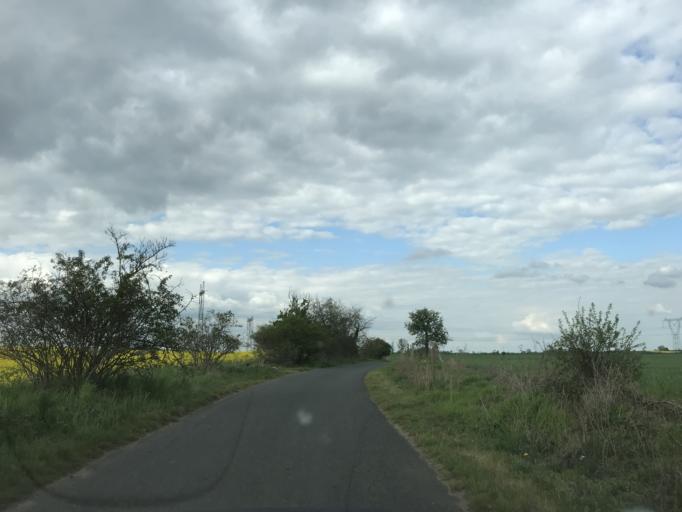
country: PL
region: West Pomeranian Voivodeship
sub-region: Powiat mysliborski
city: Mysliborz
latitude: 52.8797
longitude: 14.8948
